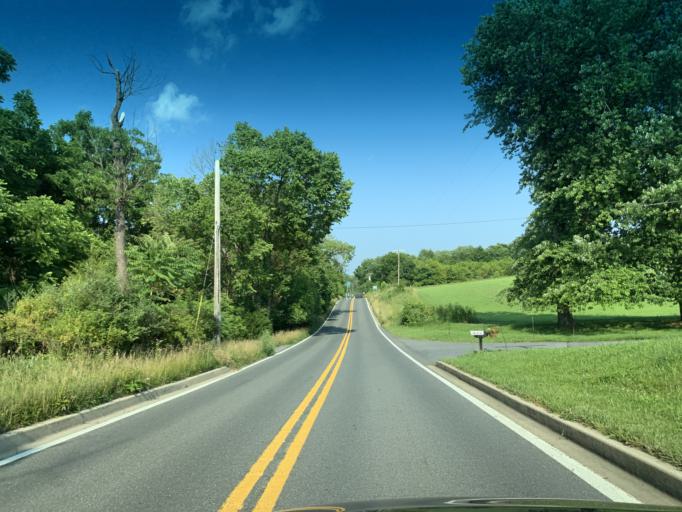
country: US
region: Maryland
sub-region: Frederick County
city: Green Valley
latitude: 39.2774
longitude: -77.3297
